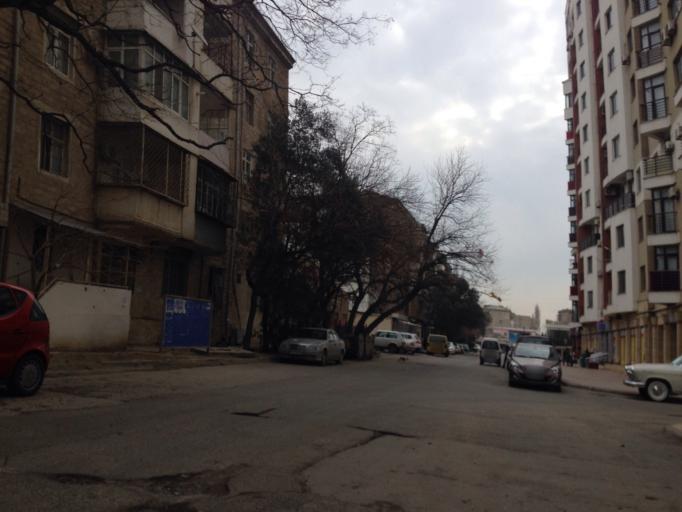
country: AZ
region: Baki
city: Baku
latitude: 40.3965
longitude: 49.8753
